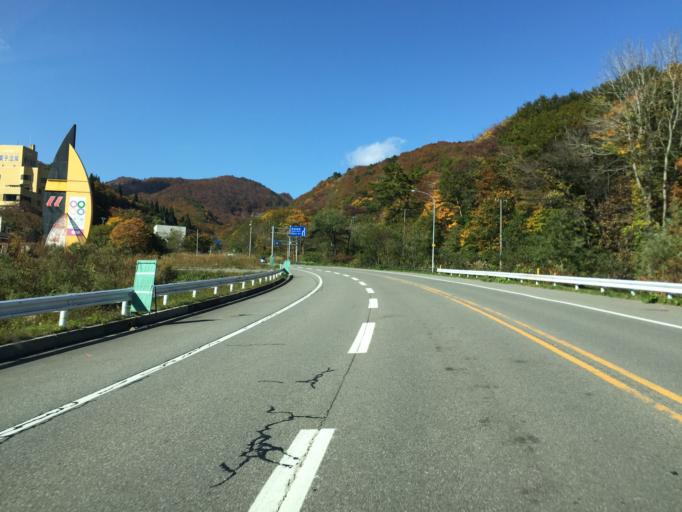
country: JP
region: Yamagata
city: Yonezawa
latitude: 37.8266
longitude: 140.2677
